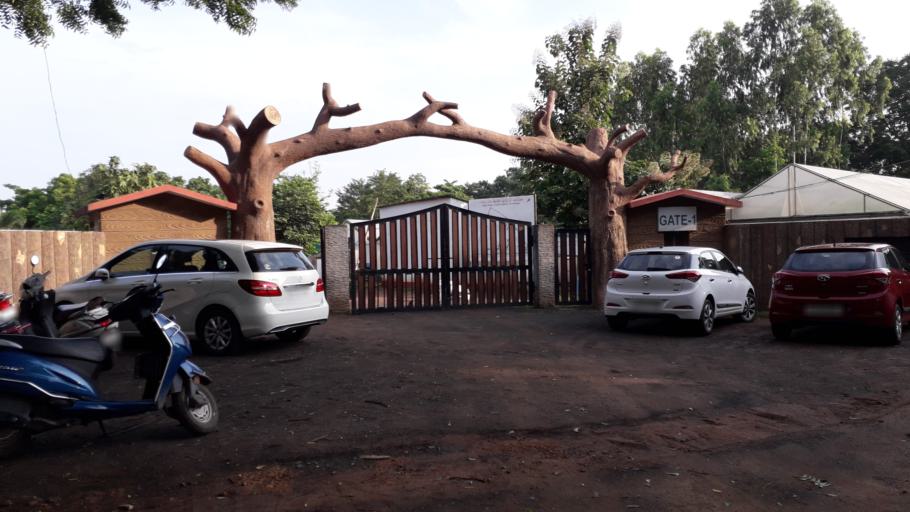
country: IN
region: Andhra Pradesh
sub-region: East Godavari
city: Rajahmundry
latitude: 17.0343
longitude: 81.8264
